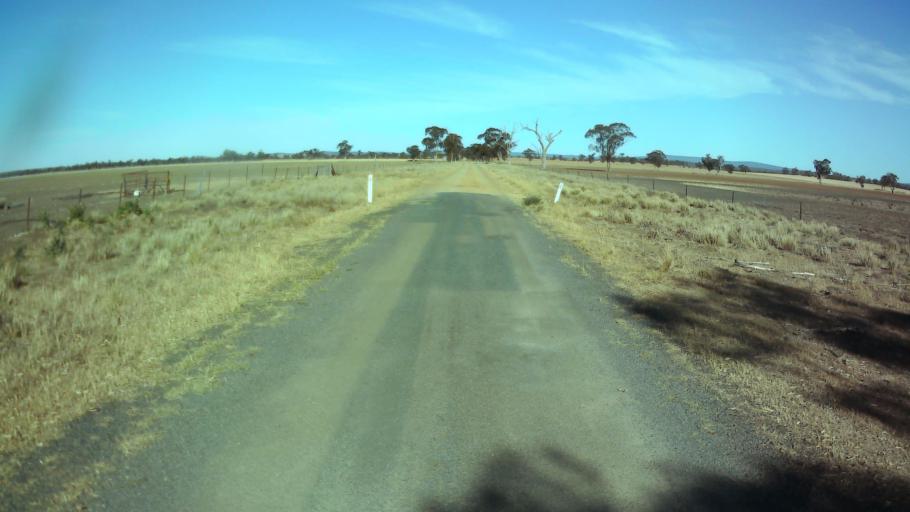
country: AU
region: New South Wales
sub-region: Weddin
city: Grenfell
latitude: -33.6584
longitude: 148.1015
